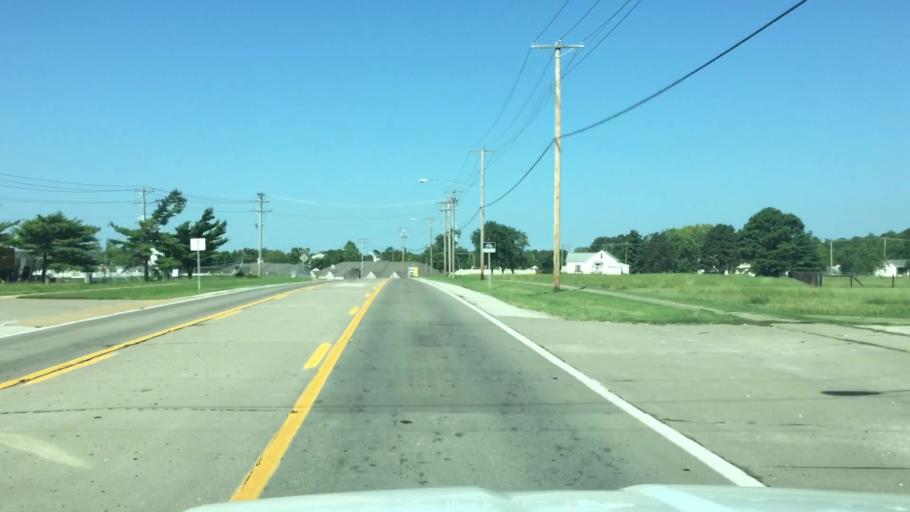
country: US
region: Missouri
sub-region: Jefferson County
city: Arnold
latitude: 38.4630
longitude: -90.3649
